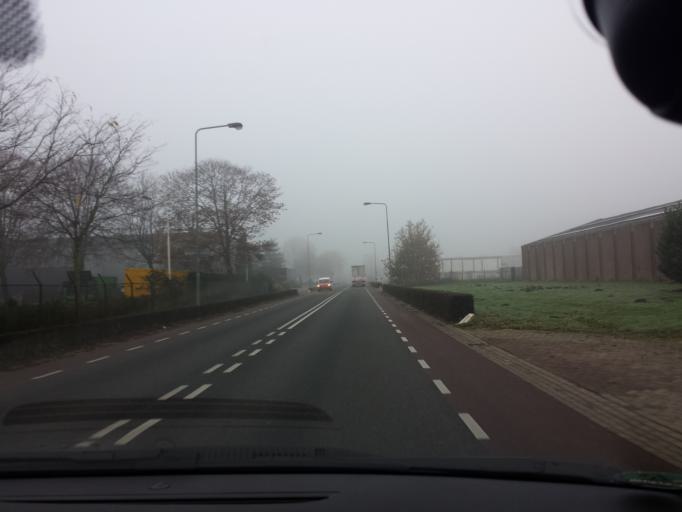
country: NL
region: Limburg
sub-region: Gemeente Peel en Maas
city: Maasbree
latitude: 51.3352
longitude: 5.9871
